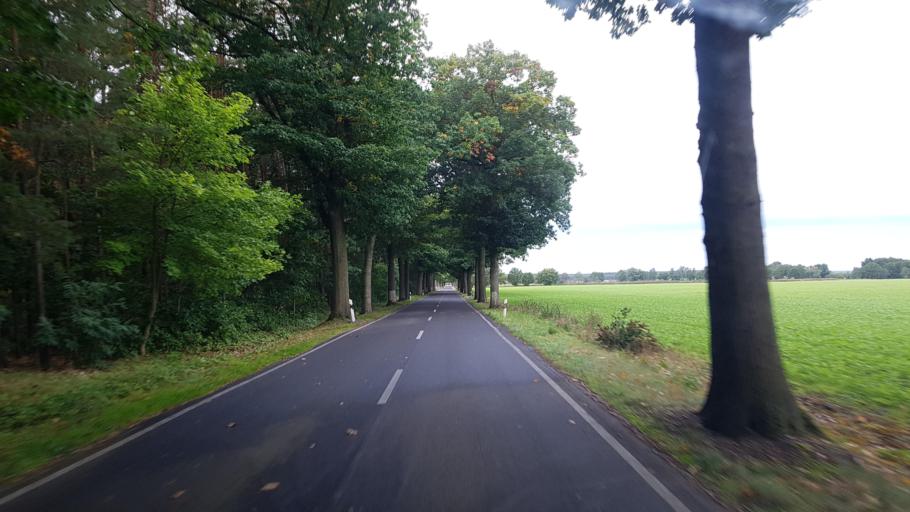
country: DE
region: Brandenburg
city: Kasel-Golzig
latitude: 51.9350
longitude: 13.6753
